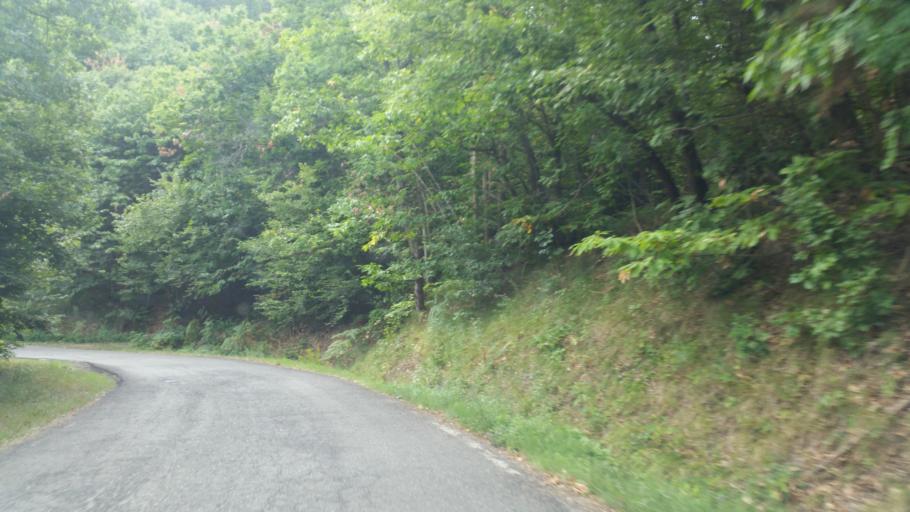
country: IT
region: Piedmont
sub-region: Provincia di Asti
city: Vesime
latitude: 44.6511
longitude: 8.2199
